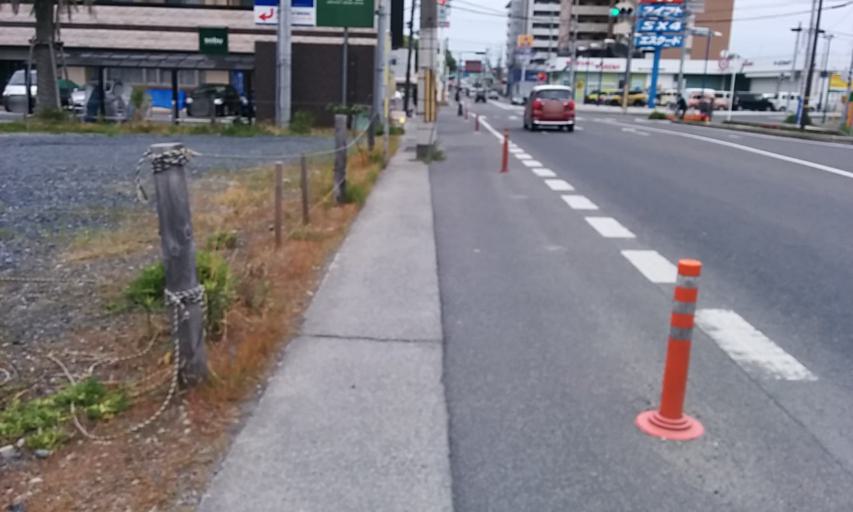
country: JP
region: Shiga Prefecture
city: Kusatsu
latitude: 35.0038
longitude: 135.9517
